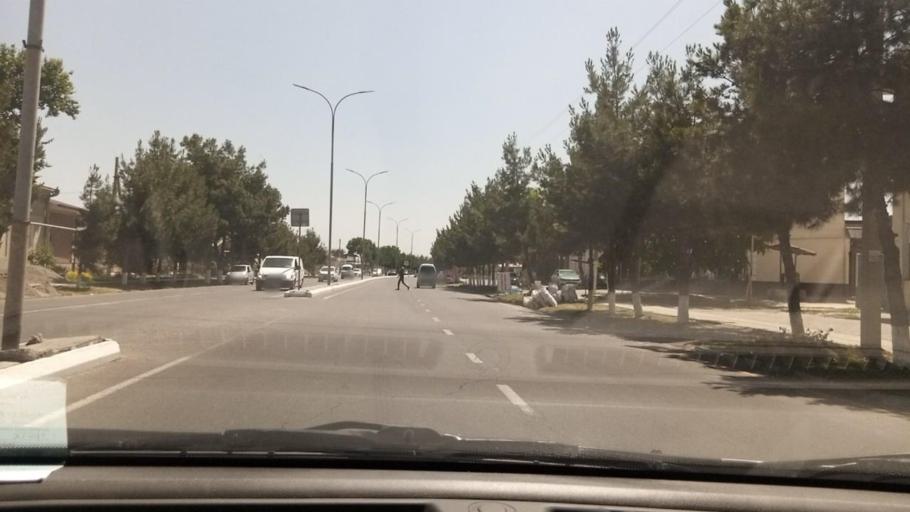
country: UZ
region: Toshkent
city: Urtaowul
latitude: 41.2119
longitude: 69.1714
